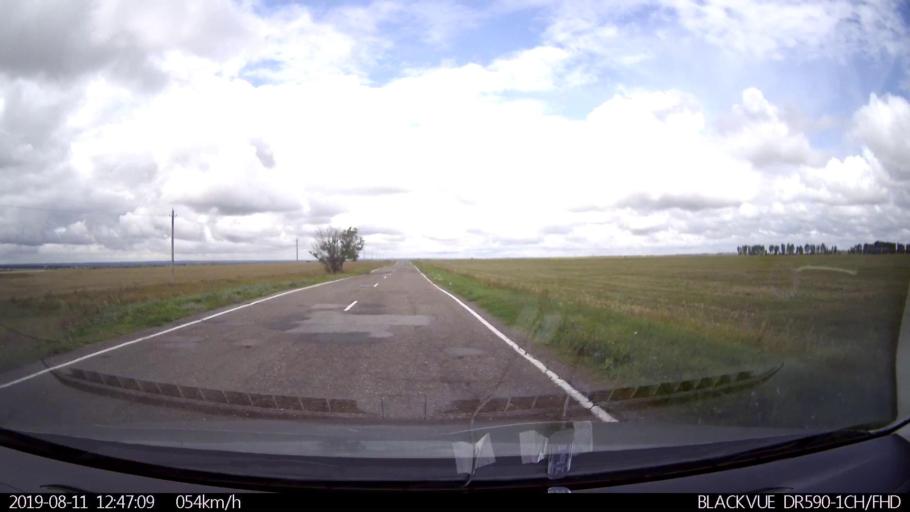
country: RU
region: Ulyanovsk
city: Ignatovka
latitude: 53.8681
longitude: 47.7115
